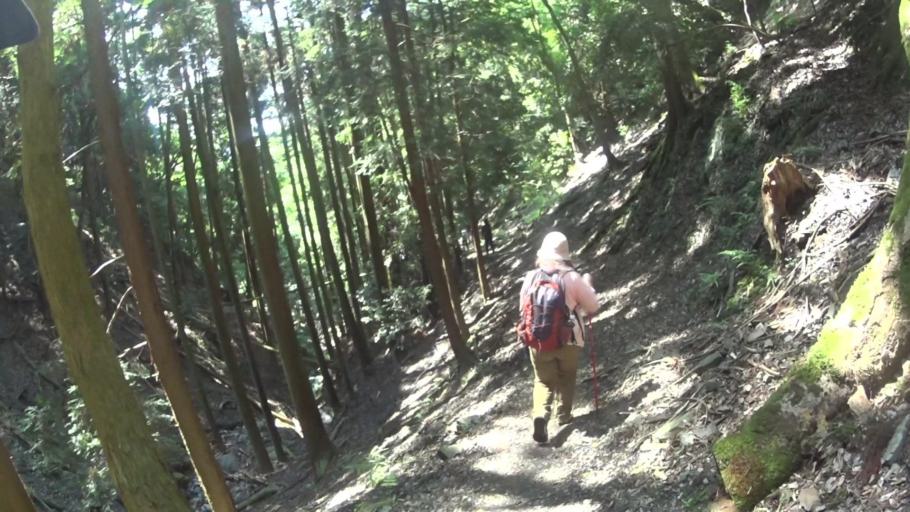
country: JP
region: Kyoto
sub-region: Kyoto-shi
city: Kamigyo-ku
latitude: 35.0194
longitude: 135.8028
